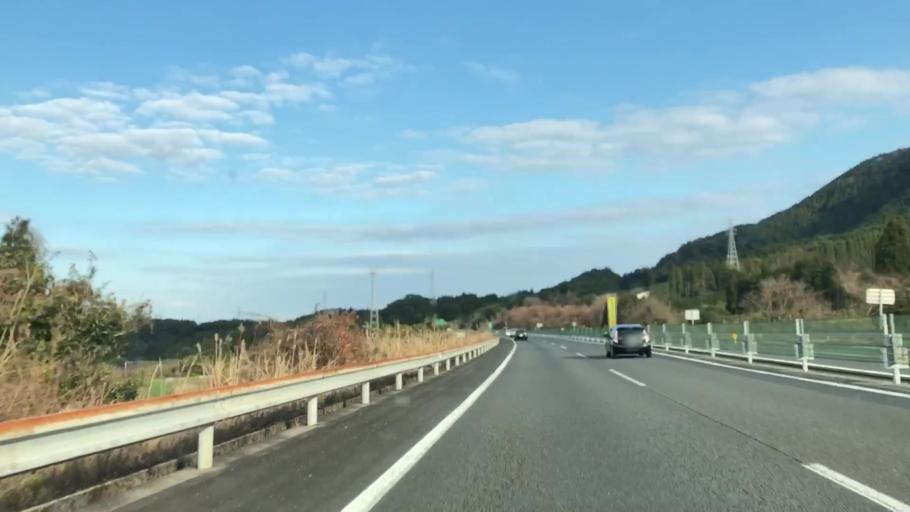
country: JP
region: Miyazaki
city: Miyazaki-shi
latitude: 31.8334
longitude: 131.3353
